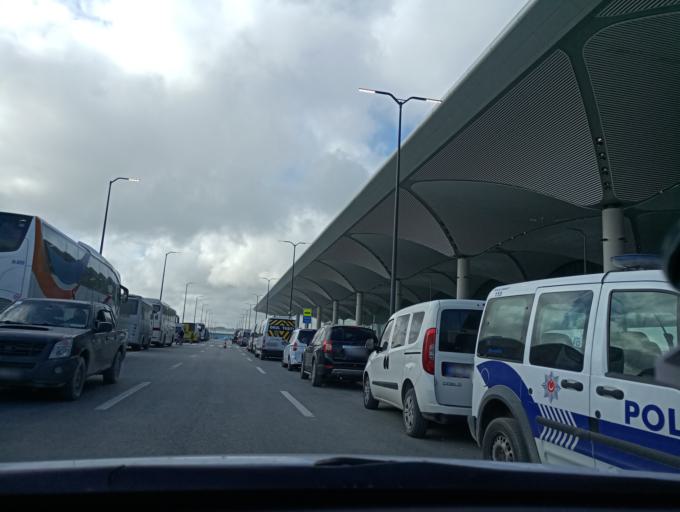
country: TR
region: Istanbul
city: Durusu
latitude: 41.2587
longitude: 28.7439
